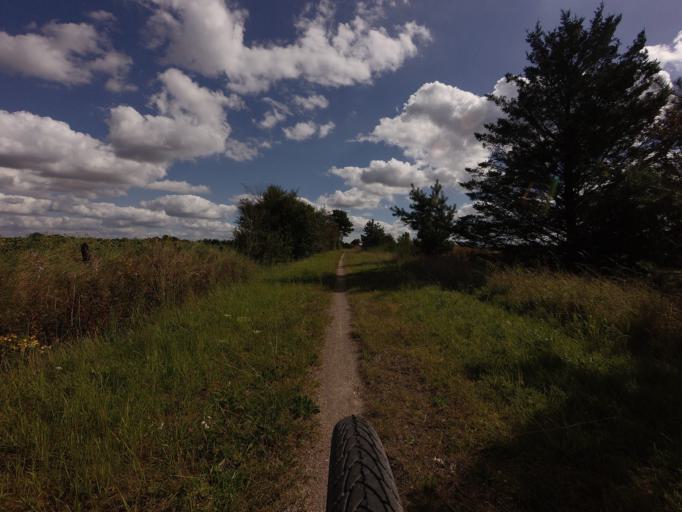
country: DK
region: Central Jutland
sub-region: Ikast-Brande Kommune
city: Brande
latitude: 55.9776
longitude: 9.1729
